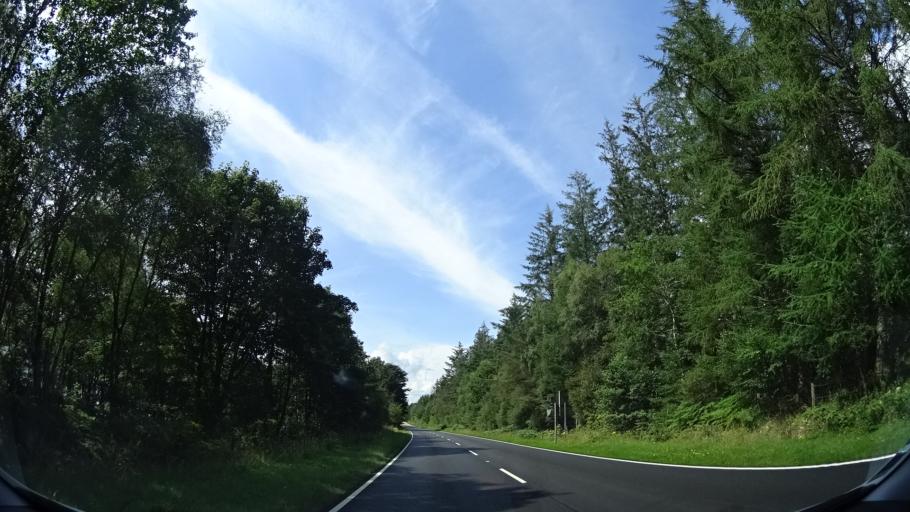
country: GB
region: Scotland
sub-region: Highland
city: Fort William
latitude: 56.8557
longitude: -5.1958
